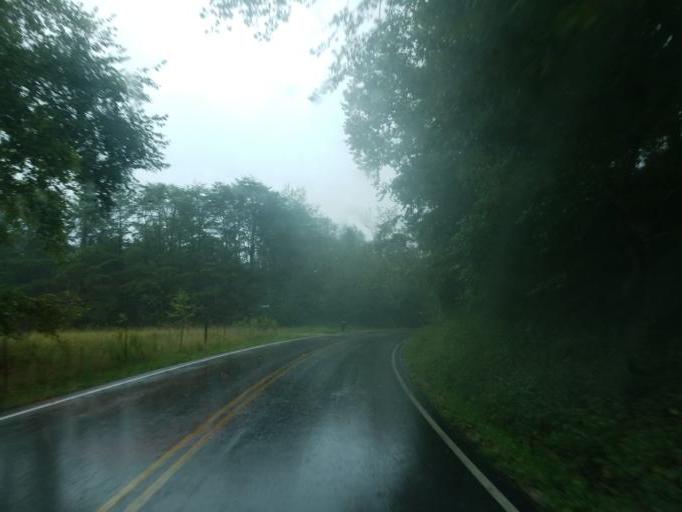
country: US
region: Kentucky
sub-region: Carter County
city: Grayson
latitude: 38.4980
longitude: -83.0011
